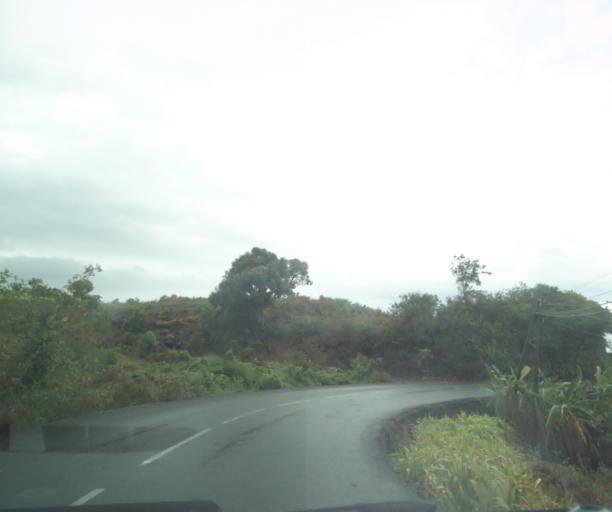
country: RE
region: Reunion
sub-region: Reunion
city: Saint-Paul
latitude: -21.0139
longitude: 55.3092
